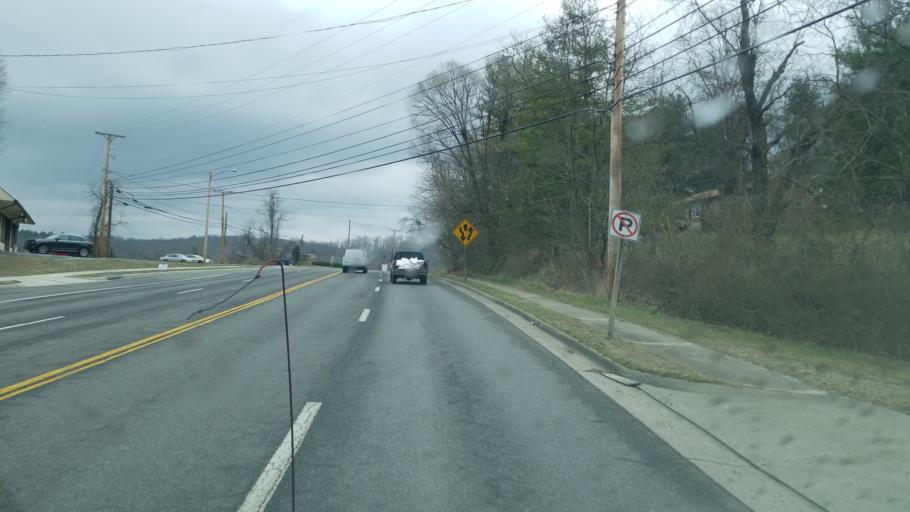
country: US
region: Virginia
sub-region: Giles County
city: Pearisburg
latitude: 37.3221
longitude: -80.7312
